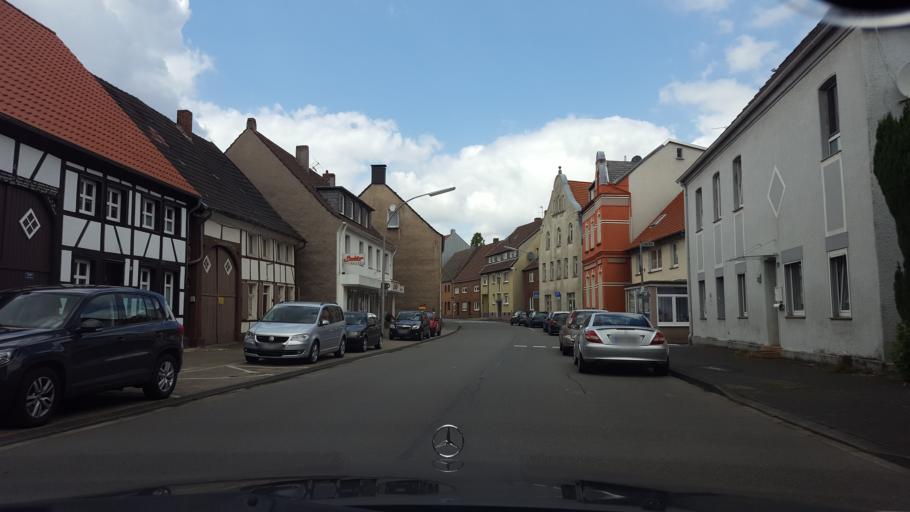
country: DE
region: North Rhine-Westphalia
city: Oer-Erkenschwick
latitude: 51.6311
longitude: 7.2941
